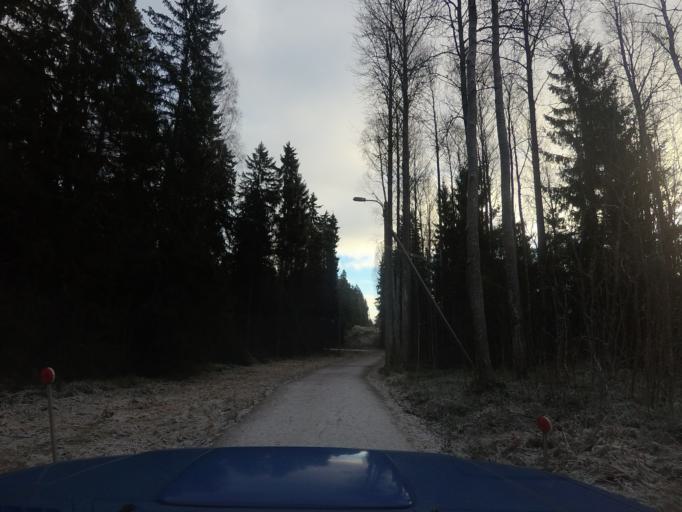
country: FI
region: Uusimaa
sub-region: Helsinki
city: Espoo
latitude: 60.1846
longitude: 24.6665
